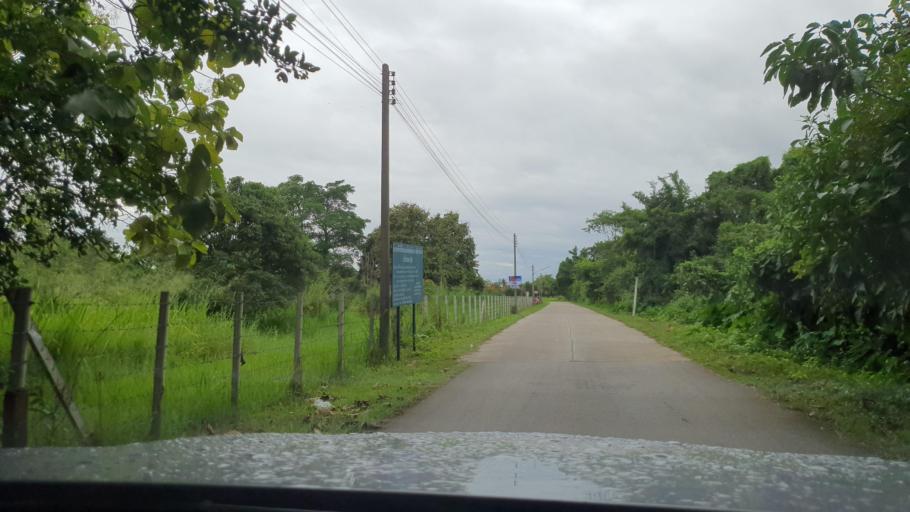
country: TH
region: Chiang Mai
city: Hang Dong
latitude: 18.6682
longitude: 98.9004
